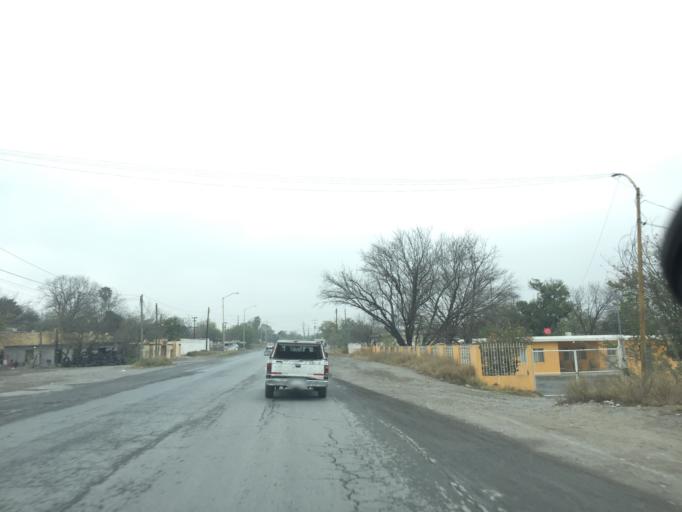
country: MX
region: Nuevo Leon
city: Mina
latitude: 25.9786
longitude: -100.4471
